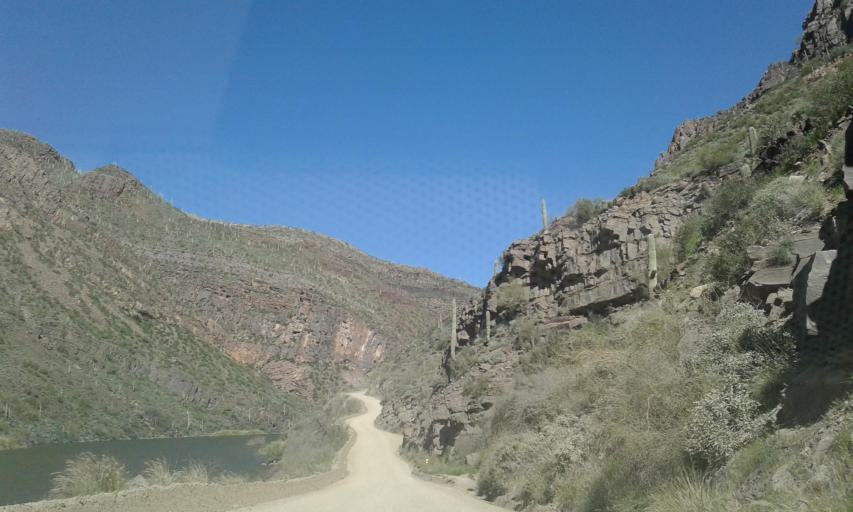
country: US
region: Arizona
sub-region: Gila County
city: Tonto Basin
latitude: 33.6632
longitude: -111.1701
